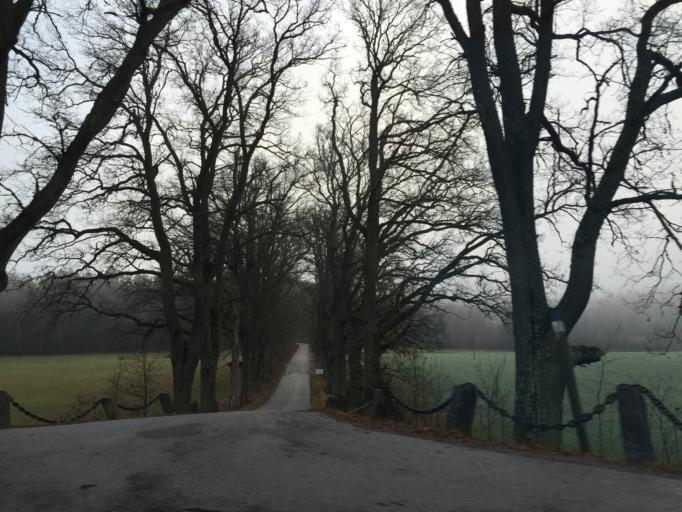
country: SE
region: Stockholm
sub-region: Botkyrka Kommun
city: Varsta
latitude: 59.1648
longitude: 17.7713
